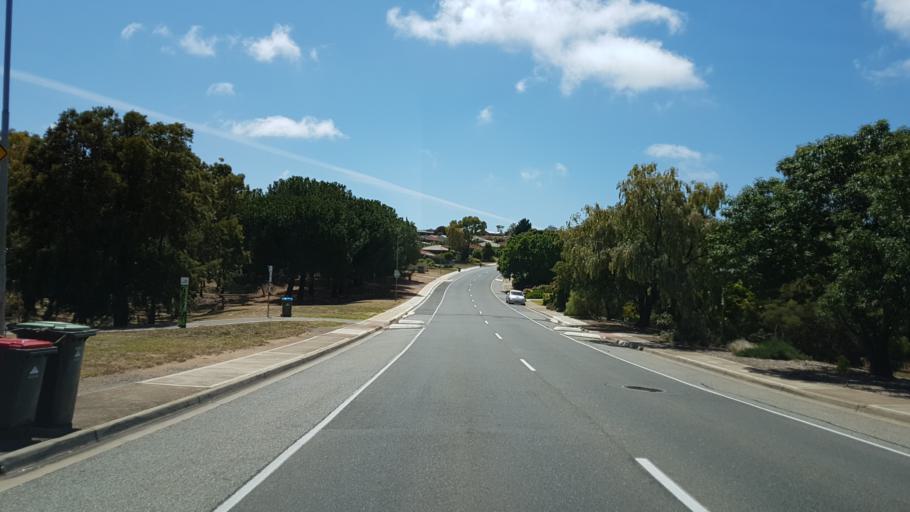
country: AU
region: South Australia
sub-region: Marion
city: Happy Valley
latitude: -35.0677
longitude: 138.5223
